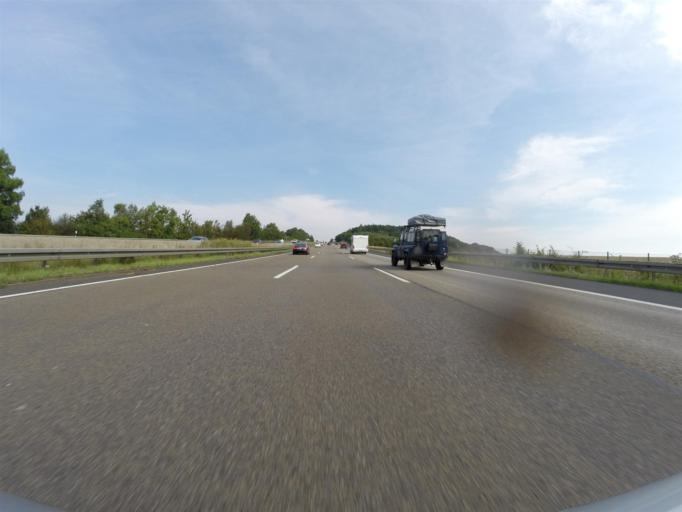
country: DE
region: Hesse
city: Schwarzenborn
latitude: 50.9433
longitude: 9.5378
